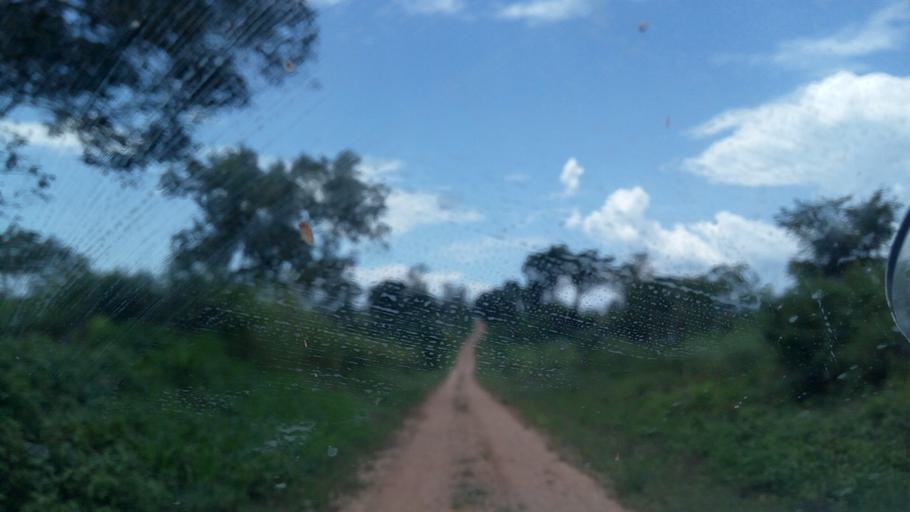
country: TZ
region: Kigoma
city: Kigoma
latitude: -4.9308
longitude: 28.7474
